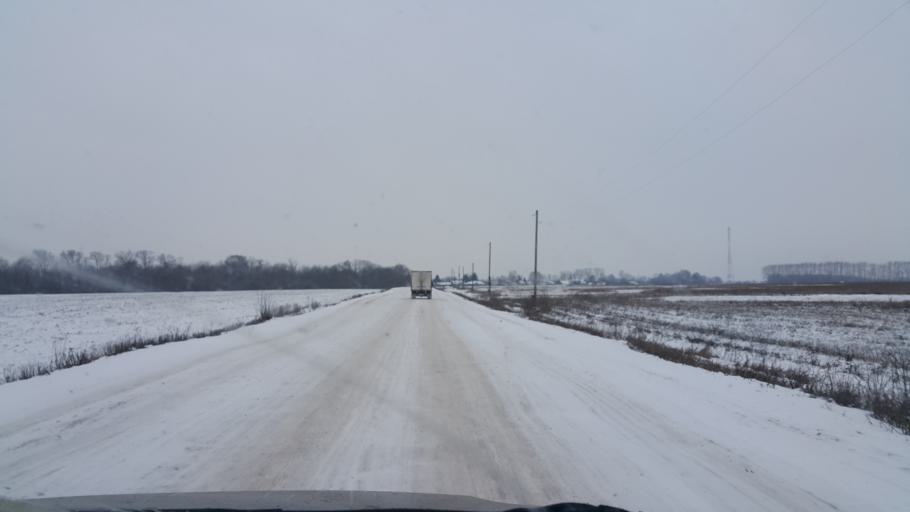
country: RU
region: Tambov
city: Inzhavino
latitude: 52.4714
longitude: 42.3960
